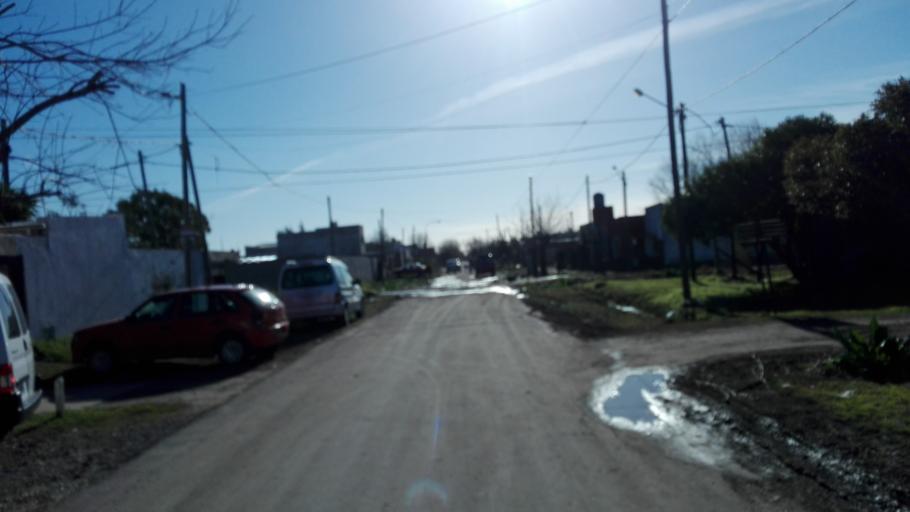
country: AR
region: Buenos Aires
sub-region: Partido de La Plata
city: La Plata
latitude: -34.8778
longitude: -57.9948
